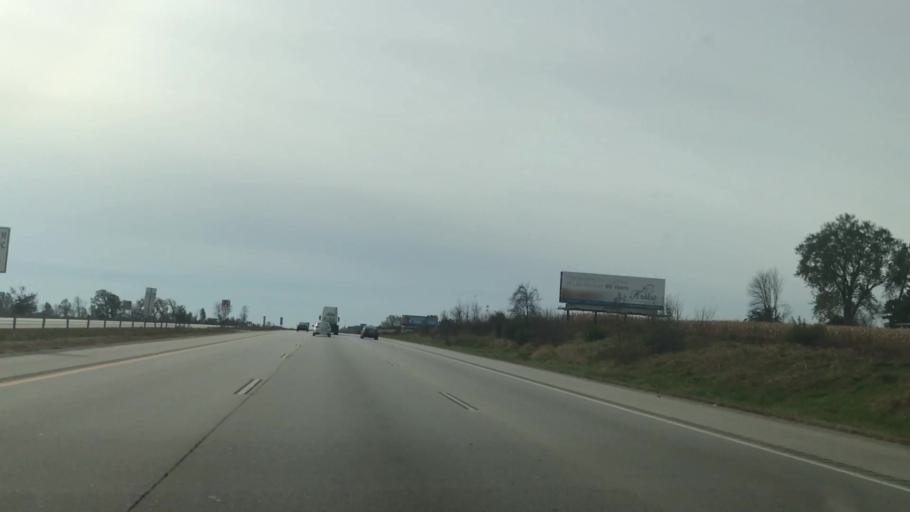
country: US
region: Wisconsin
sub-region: Washington County
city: Richfield
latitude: 43.2611
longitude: -88.1819
